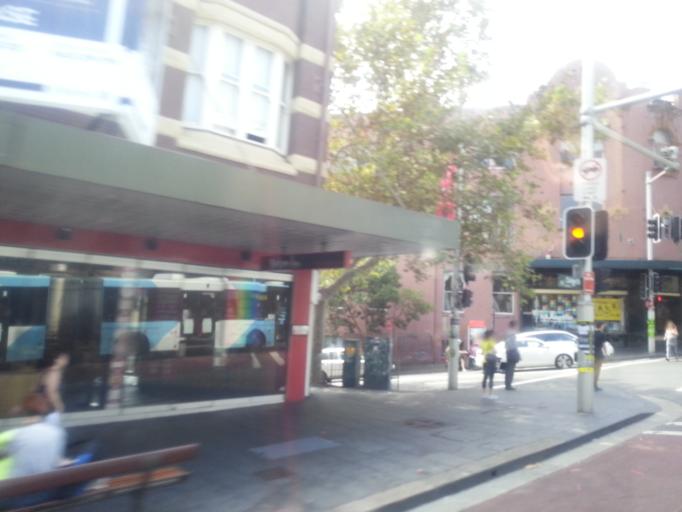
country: AU
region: New South Wales
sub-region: City of Sydney
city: Darlinghurst
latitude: -33.8789
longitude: 151.2149
